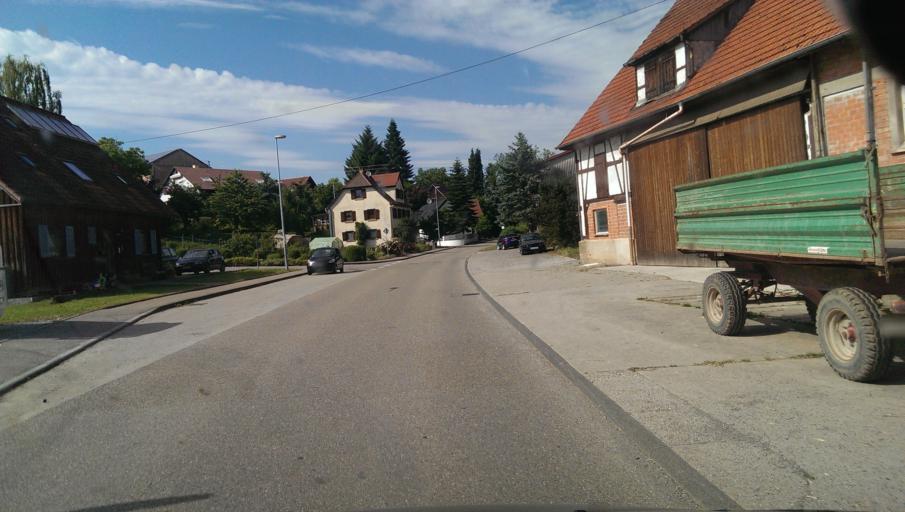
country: DE
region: Baden-Wuerttemberg
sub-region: Regierungsbezirk Stuttgart
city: Zweiflingen
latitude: 49.2329
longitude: 9.4965
